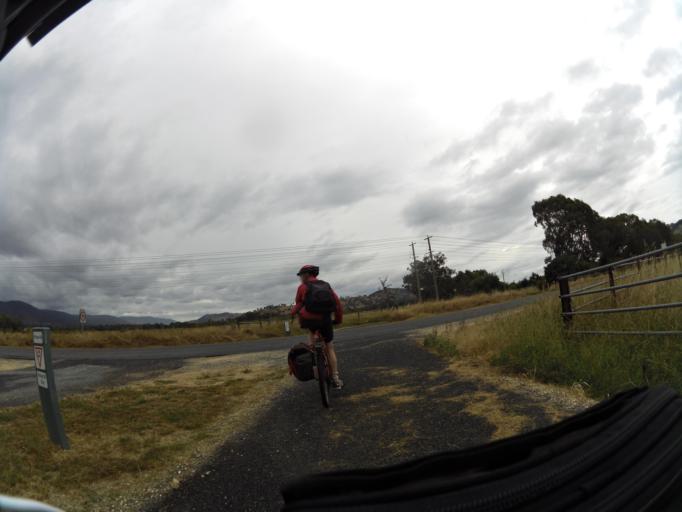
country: AU
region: New South Wales
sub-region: Albury Municipality
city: East Albury
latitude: -36.1509
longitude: 146.9574
